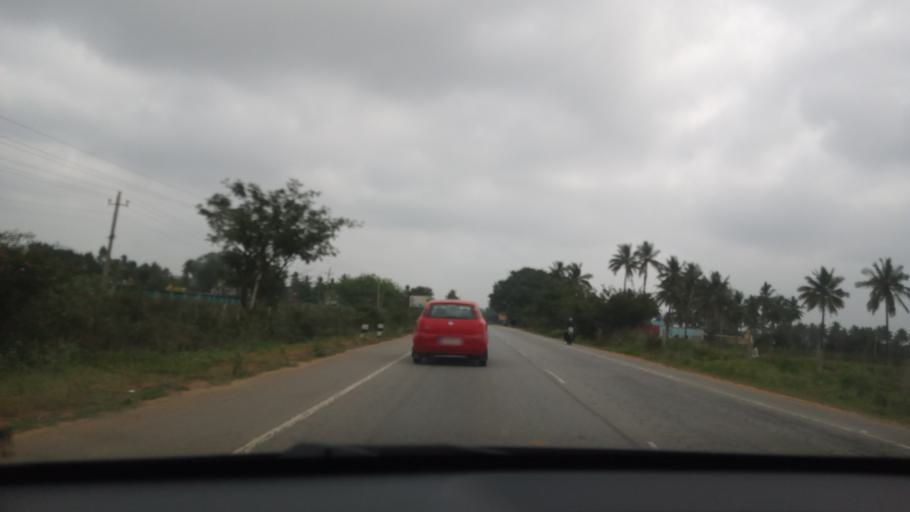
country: IN
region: Karnataka
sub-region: Chikkaballapur
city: Chintamani
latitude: 13.3474
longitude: 78.0203
